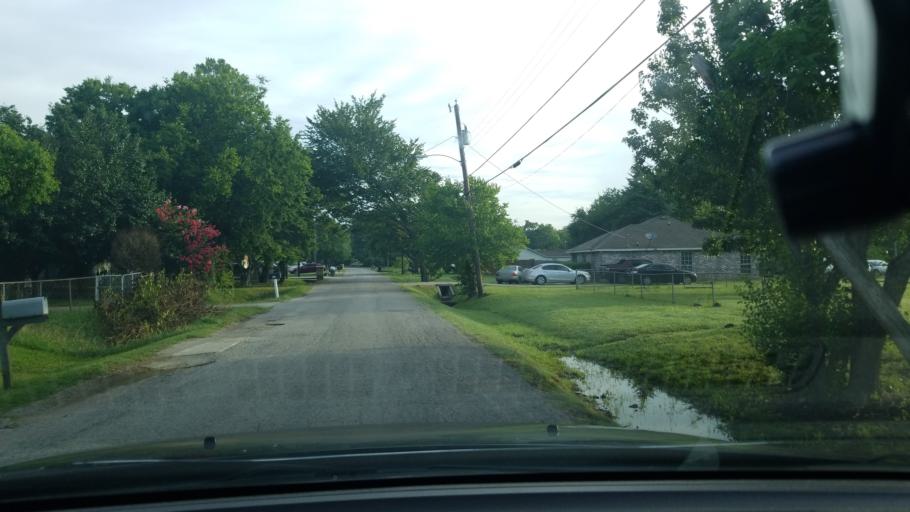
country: US
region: Texas
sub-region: Dallas County
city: Balch Springs
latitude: 32.7602
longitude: -96.6409
